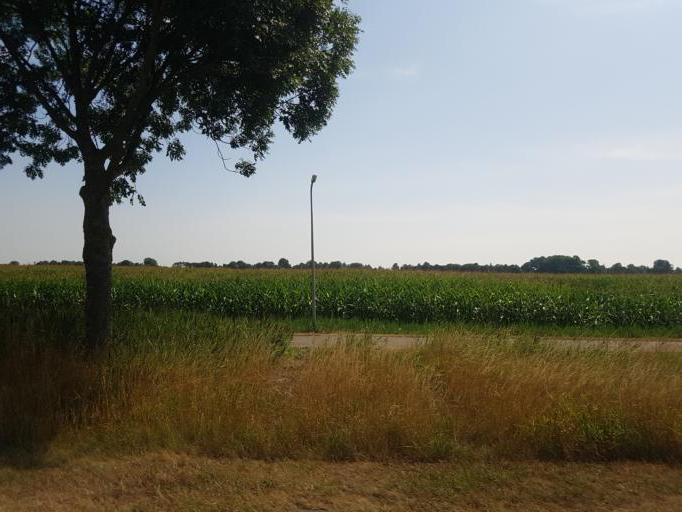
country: NL
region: Overijssel
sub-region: Gemeente Steenwijkerland
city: Giethoorn
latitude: 52.7284
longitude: 6.0773
